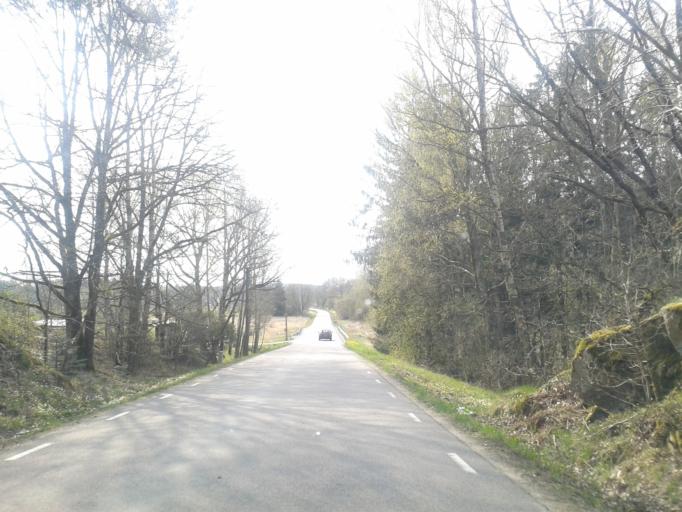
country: SE
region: Vaestra Goetaland
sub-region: Kungalvs Kommun
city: Kode
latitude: 57.9091
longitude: 11.8908
